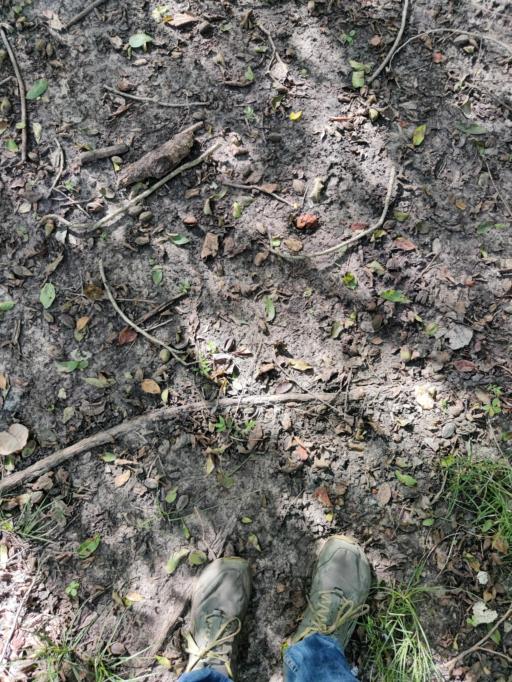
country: US
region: Texas
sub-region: Harris County
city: Oak Cliff Place
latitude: 29.8338
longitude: -95.6643
